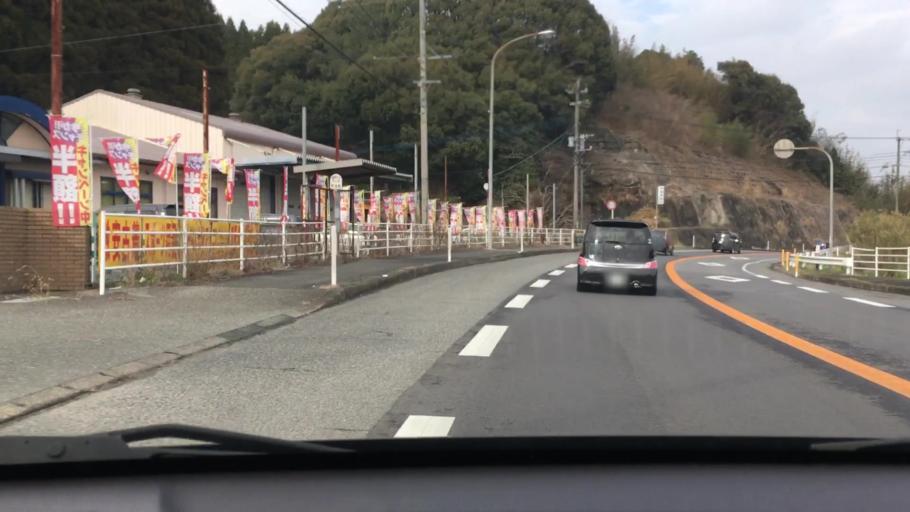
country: JP
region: Saga Prefecture
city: Imaricho-ko
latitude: 33.3199
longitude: 129.9287
